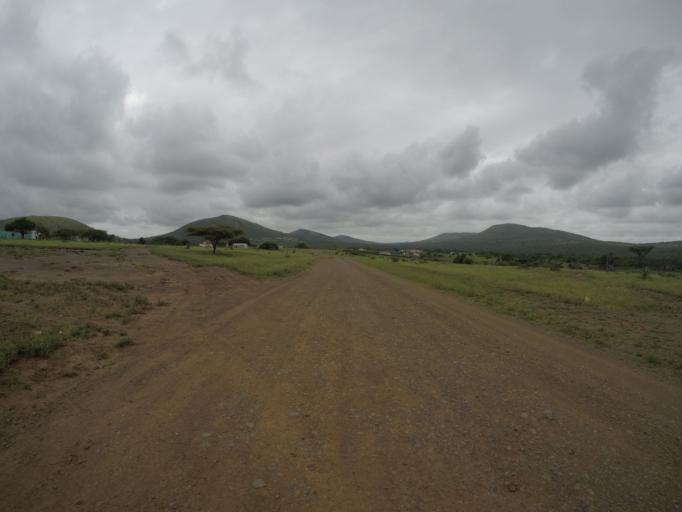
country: ZA
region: KwaZulu-Natal
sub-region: uThungulu District Municipality
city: Empangeni
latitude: -28.6086
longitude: 31.8681
